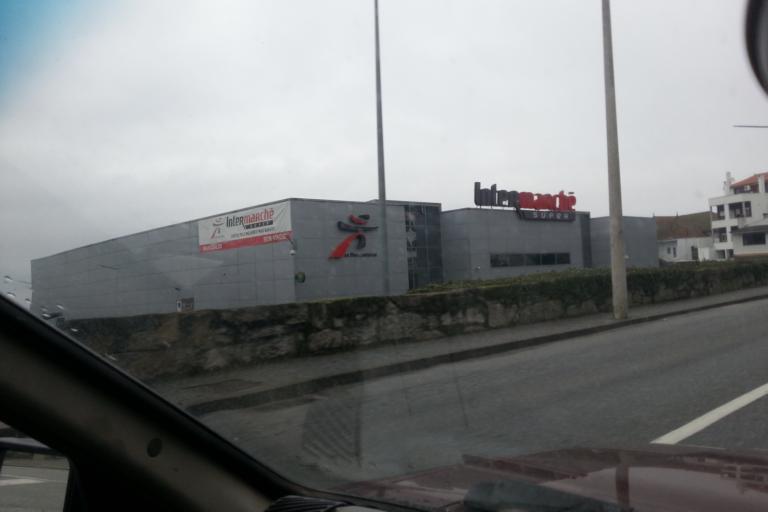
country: PT
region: Viseu
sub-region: Mangualde
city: Mangualde
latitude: 40.6043
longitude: -7.7686
